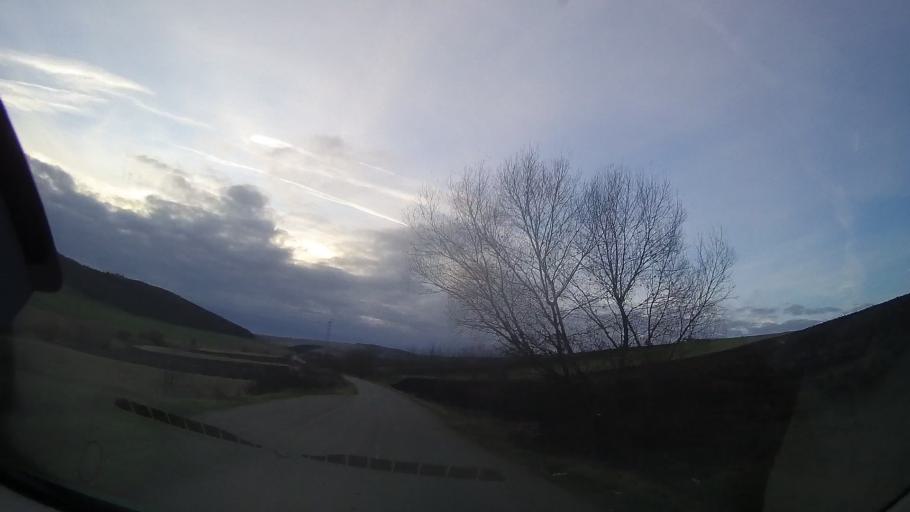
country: RO
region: Cluj
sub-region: Comuna Geaca
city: Geaca
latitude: 46.8540
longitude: 24.0801
